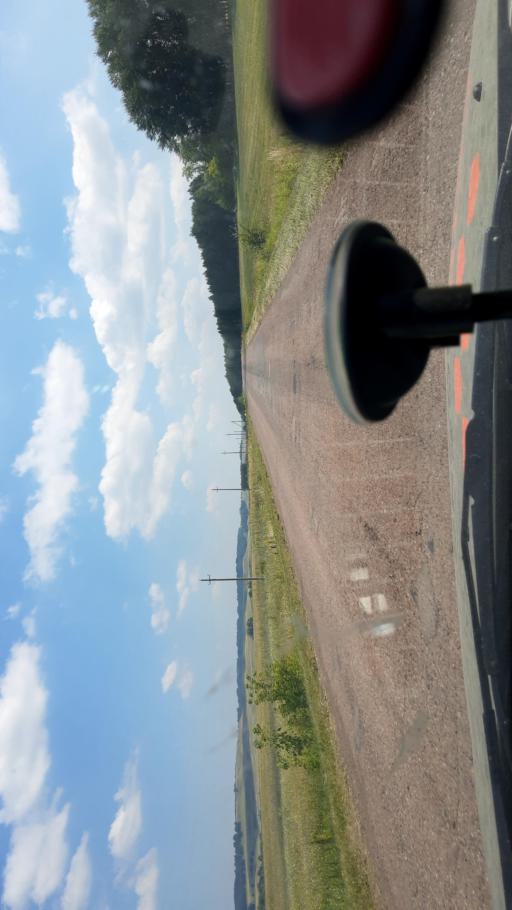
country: RU
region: Bashkortostan
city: Chekmagush
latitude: 54.8871
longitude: 54.5848
